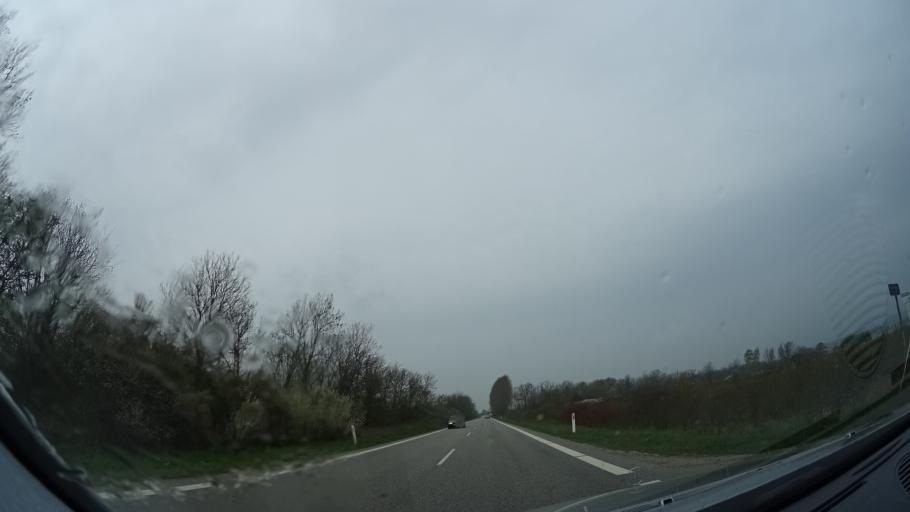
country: DK
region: Zealand
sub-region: Holbaek Kommune
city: Holbaek
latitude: 55.7149
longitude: 11.6547
